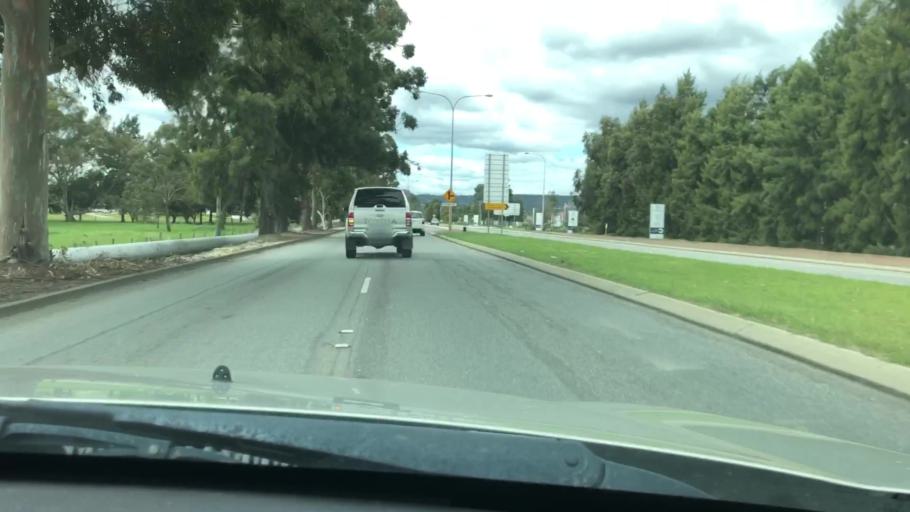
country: AU
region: Western Australia
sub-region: Armadale
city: Seville Grove
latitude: -32.1471
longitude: 115.9755
